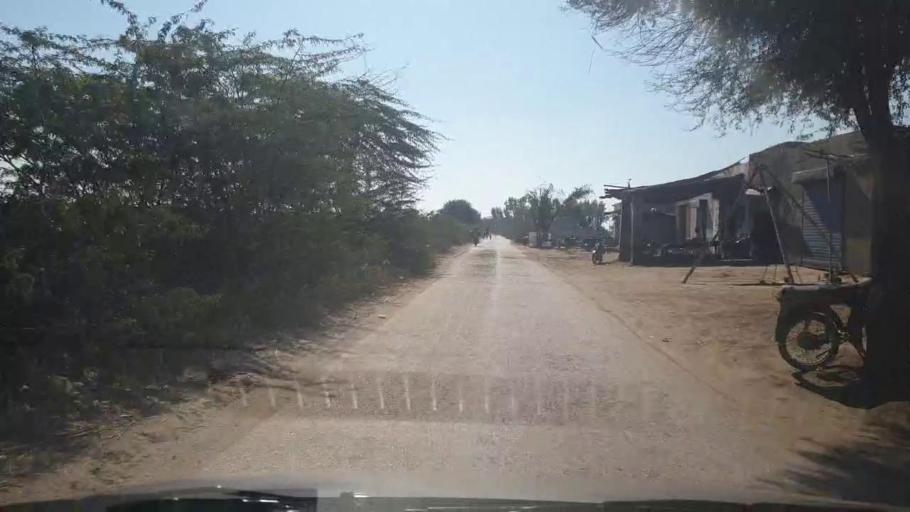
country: PK
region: Sindh
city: Bozdar
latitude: 27.1799
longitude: 68.6394
